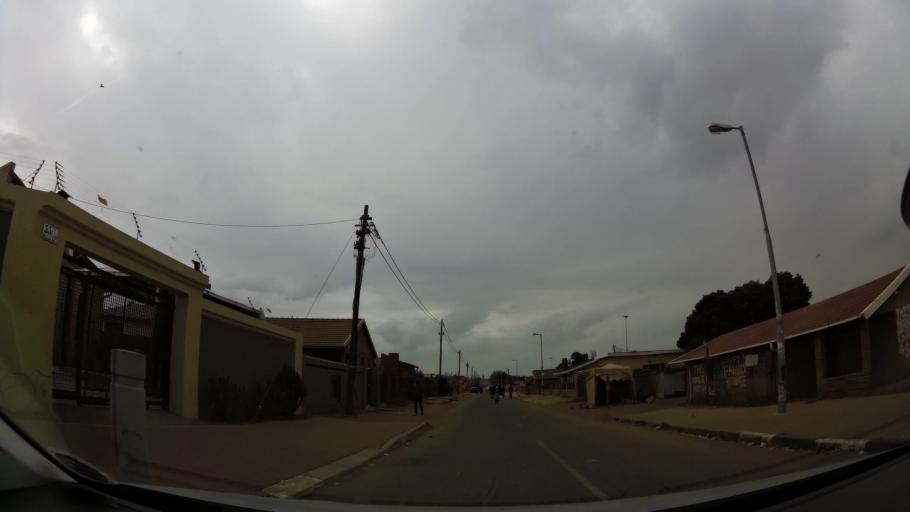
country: ZA
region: Gauteng
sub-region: City of Johannesburg Metropolitan Municipality
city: Soweto
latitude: -26.2593
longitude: 27.8653
